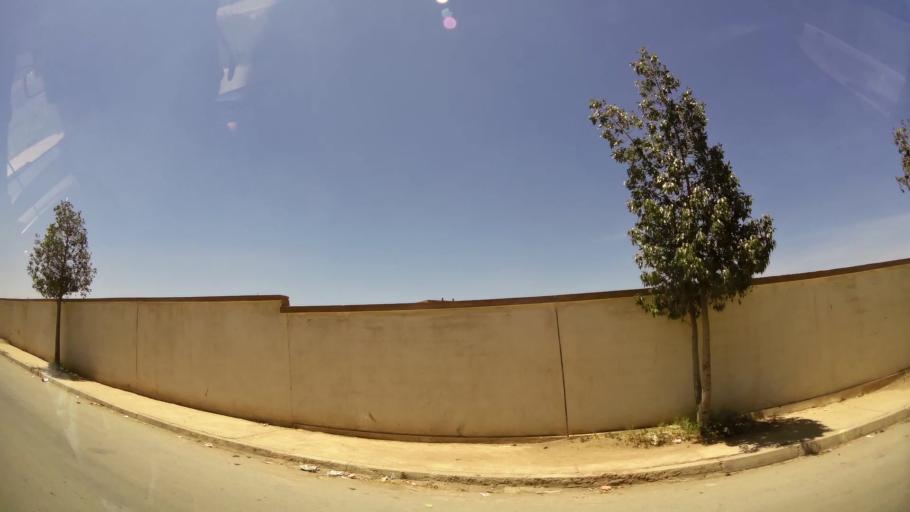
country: MA
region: Oriental
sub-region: Oujda-Angad
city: Oujda
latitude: 34.6668
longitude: -1.9252
